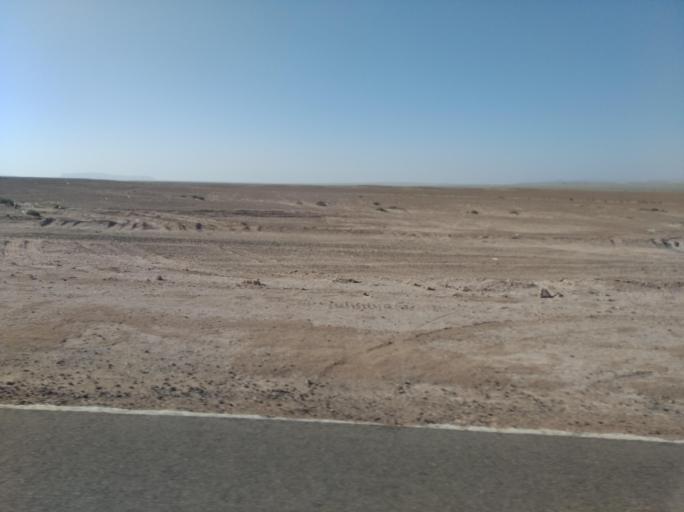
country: CL
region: Atacama
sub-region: Provincia de Copiapo
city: Copiapo
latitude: -27.3166
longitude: -70.8381
